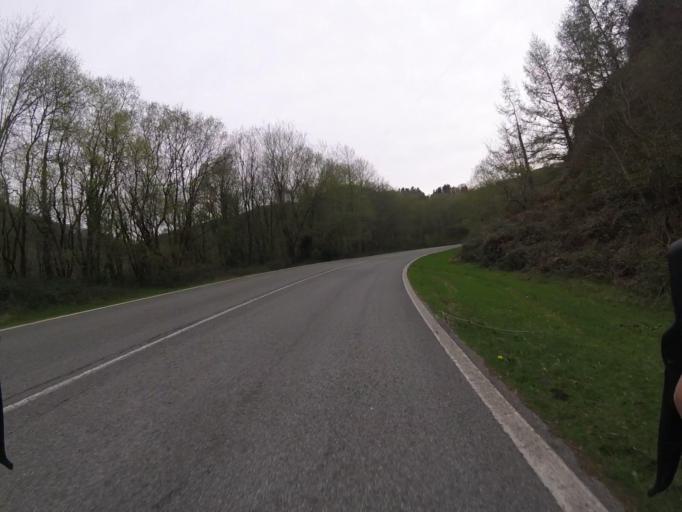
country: ES
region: Basque Country
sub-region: Provincia de Guipuzcoa
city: Irun
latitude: 43.2765
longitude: -1.7752
